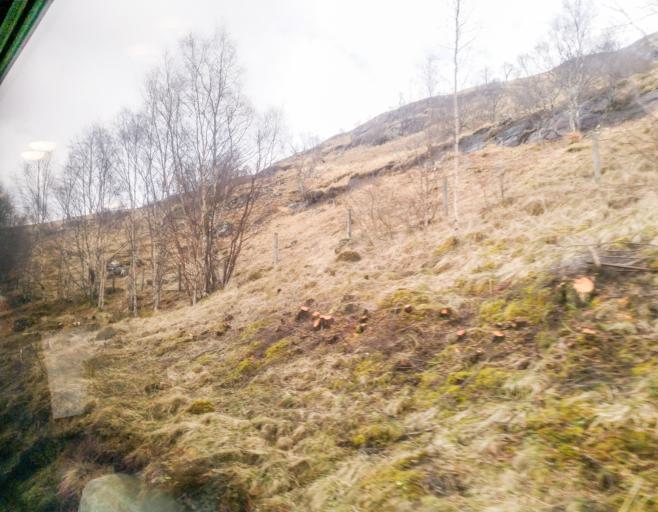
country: GB
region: Scotland
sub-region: Highland
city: Spean Bridge
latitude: 56.7902
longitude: -4.7277
